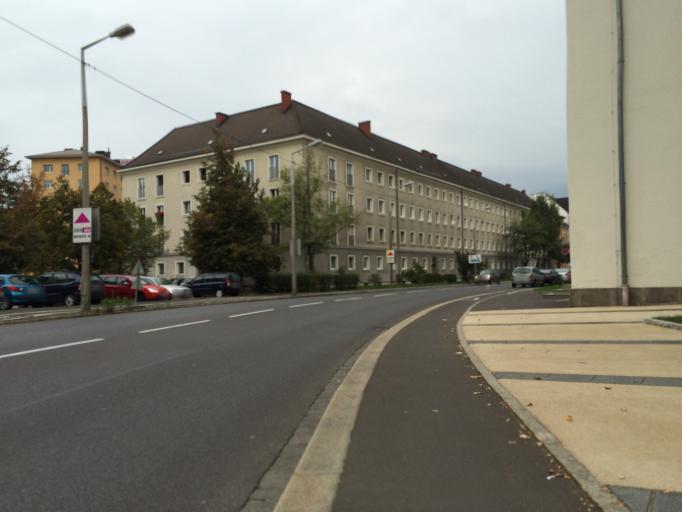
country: AT
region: Upper Austria
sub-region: Linz Stadt
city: Linz
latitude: 48.2884
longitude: 14.3021
